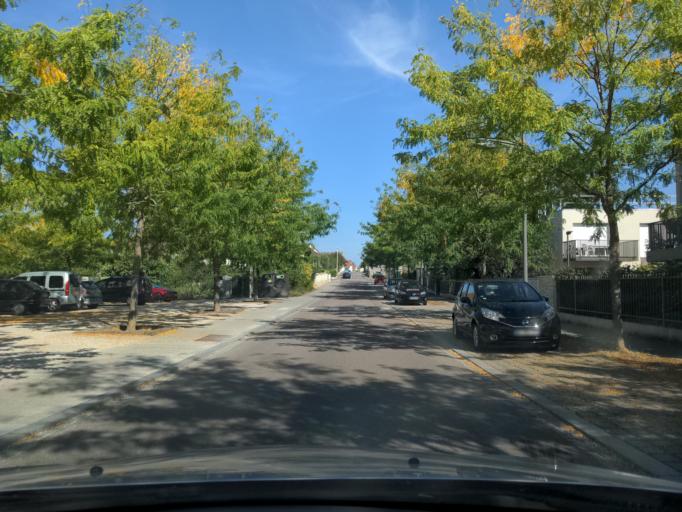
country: FR
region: Bourgogne
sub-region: Departement de la Cote-d'Or
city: Saint-Apollinaire
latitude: 47.3289
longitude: 5.0830
